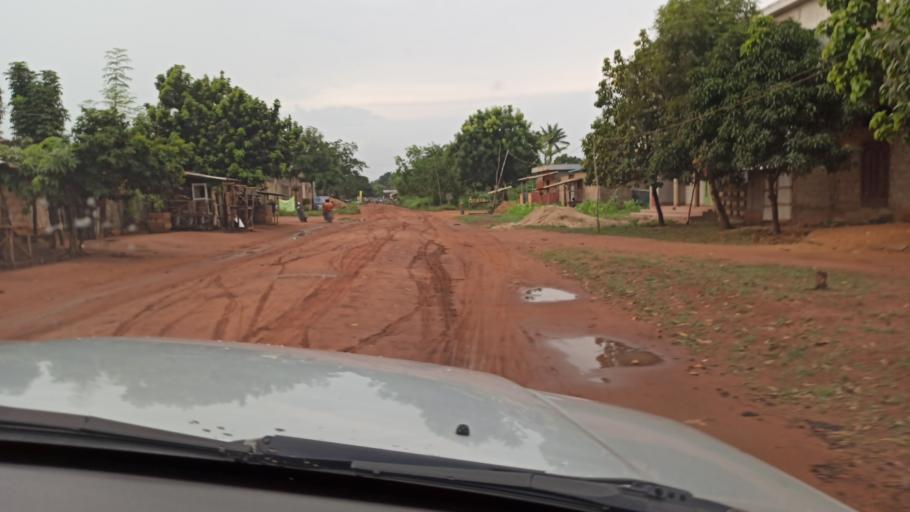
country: BJ
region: Queme
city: Porto-Novo
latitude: 6.4882
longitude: 2.6667
